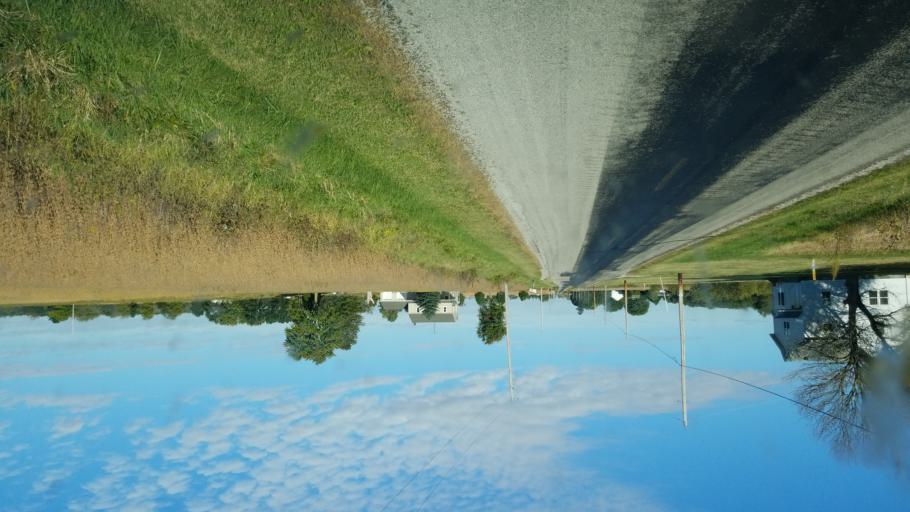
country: US
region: Ohio
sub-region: Crawford County
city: Bucyrus
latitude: 40.6889
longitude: -82.9820
